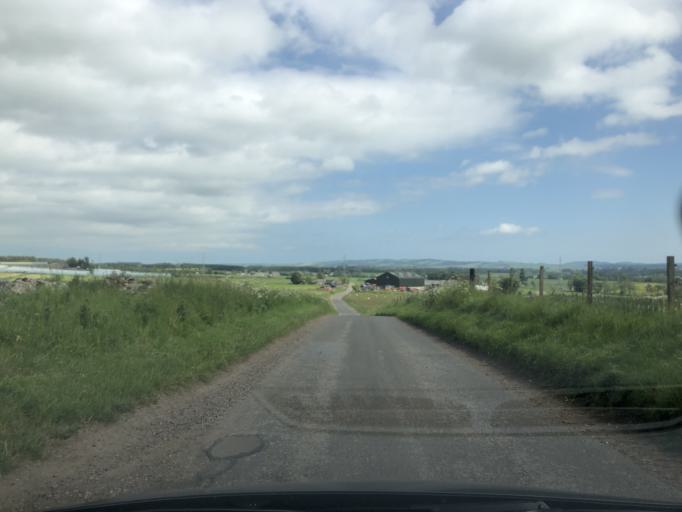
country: GB
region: Scotland
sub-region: Angus
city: Kirriemuir
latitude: 56.7227
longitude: -2.9619
